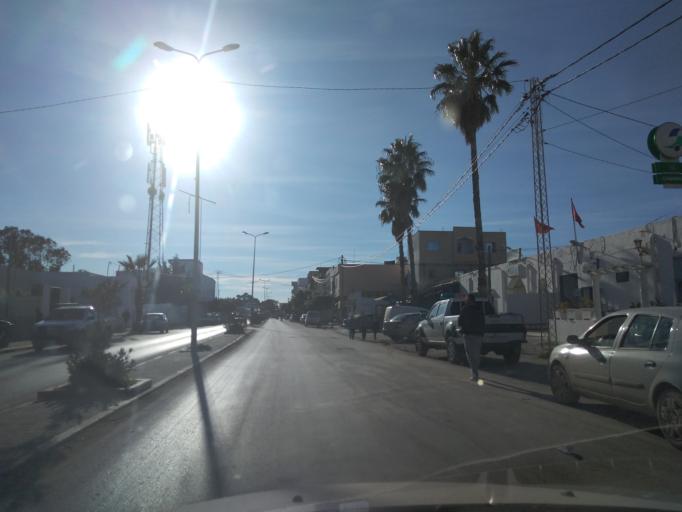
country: TN
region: Ariana
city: Qal'at al Andalus
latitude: 37.0587
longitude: 10.1101
